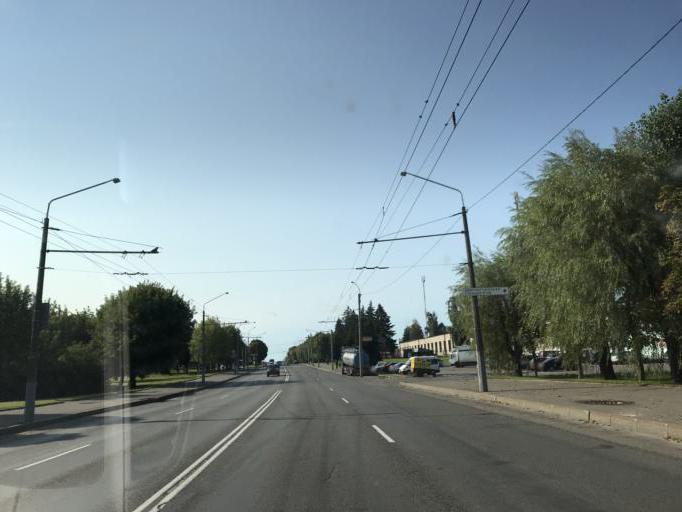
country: BY
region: Mogilev
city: Buynichy
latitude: 53.8800
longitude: 30.2667
